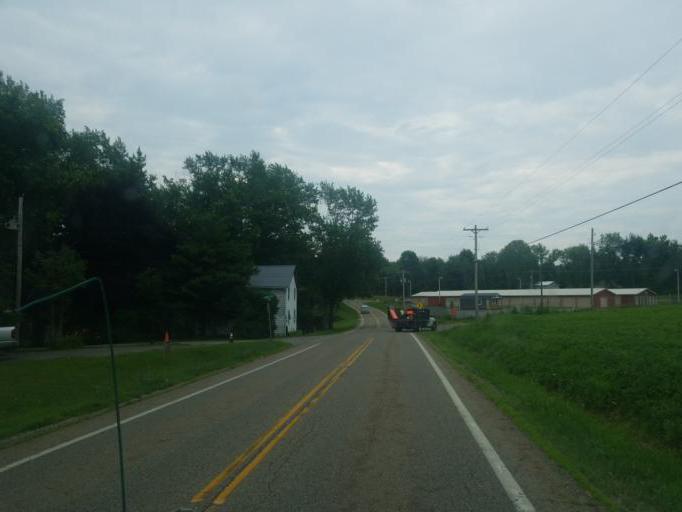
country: US
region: Ohio
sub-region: Carroll County
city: Lake Mohawk
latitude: 40.6347
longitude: -81.2142
